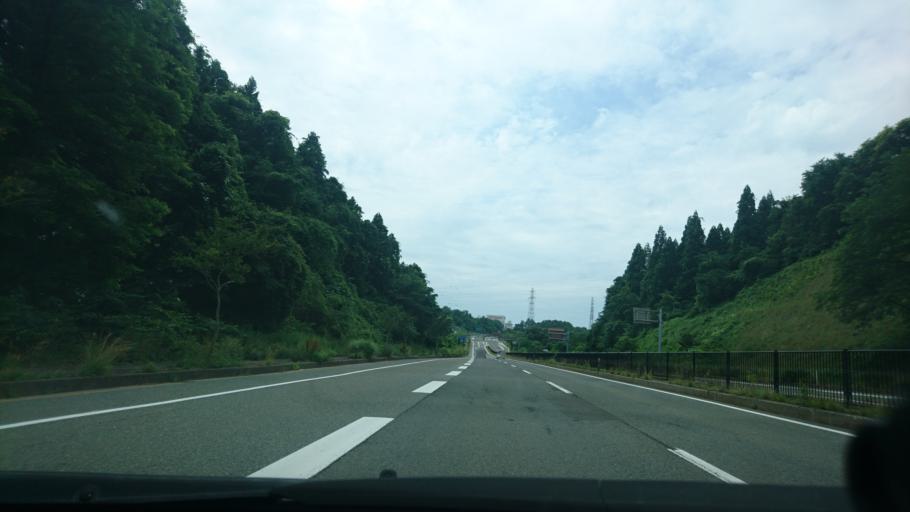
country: JP
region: Akita
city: Akita
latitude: 39.6631
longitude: 140.1842
